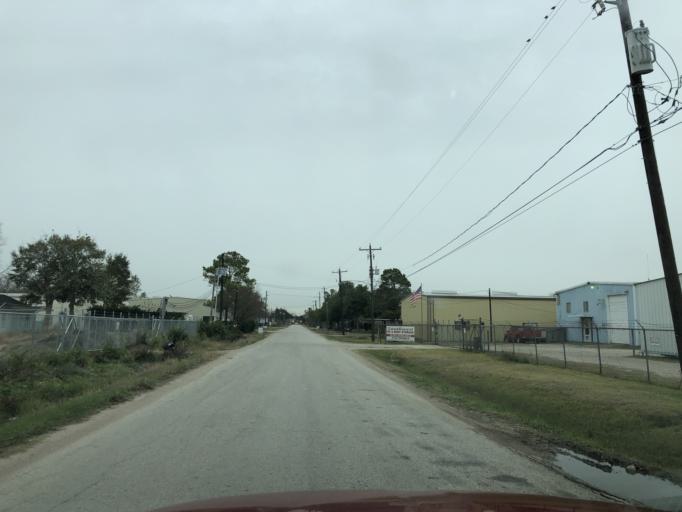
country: US
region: Texas
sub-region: Fort Bend County
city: Missouri City
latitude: 29.6330
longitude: -95.5223
